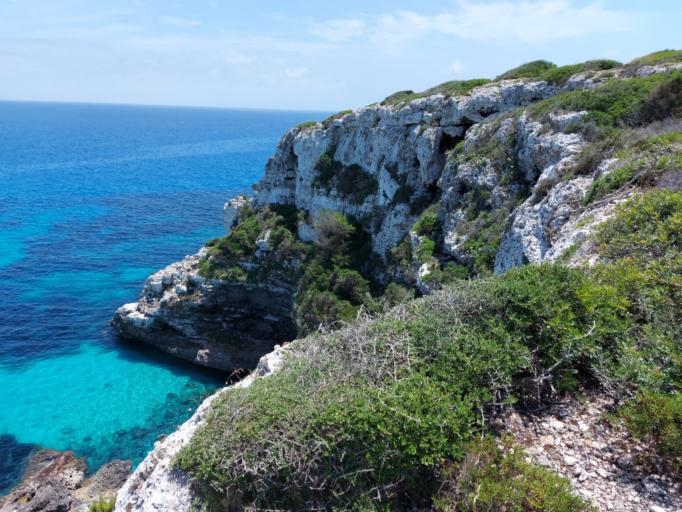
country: ES
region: Balearic Islands
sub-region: Illes Balears
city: Ses Salines
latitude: 39.2883
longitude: 3.0906
